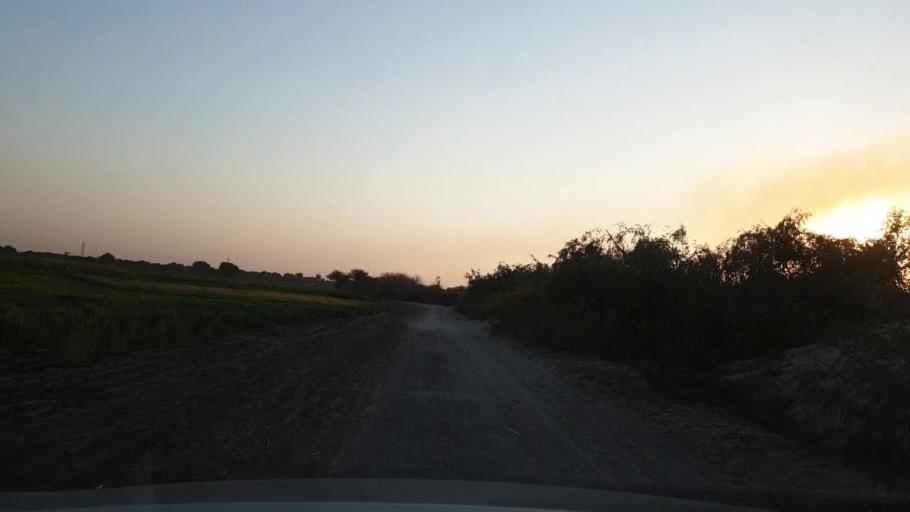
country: PK
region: Sindh
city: Tando Allahyar
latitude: 25.5495
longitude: 68.6377
